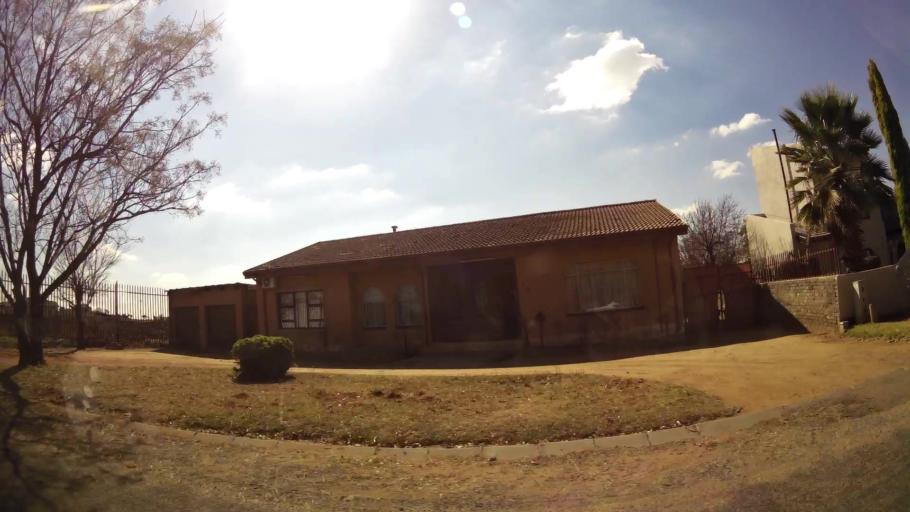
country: ZA
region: Gauteng
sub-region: West Rand District Municipality
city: Randfontein
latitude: -26.1663
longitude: 27.7500
